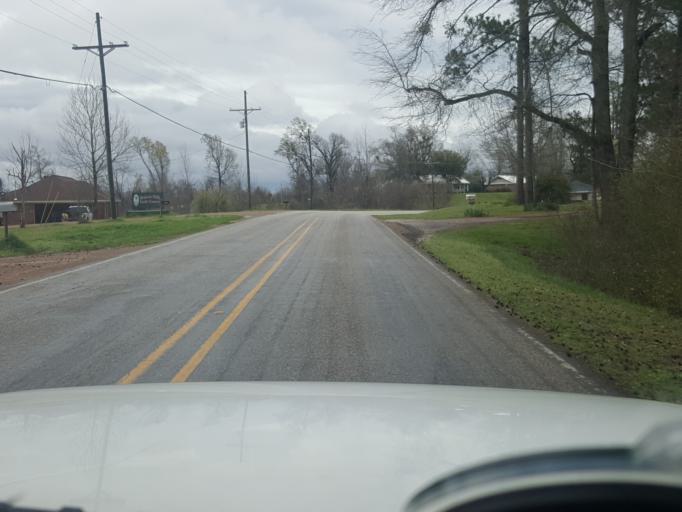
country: US
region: Mississippi
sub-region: Yazoo County
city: Yazoo City
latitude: 32.8425
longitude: -90.3499
